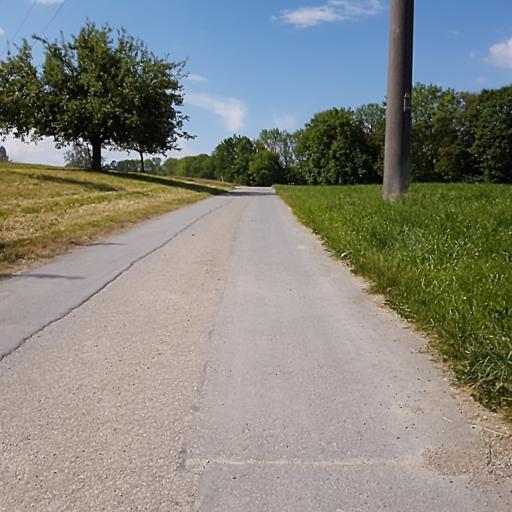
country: CH
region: Thurgau
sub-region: Arbon District
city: Amriswil
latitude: 47.5584
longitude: 9.3004
